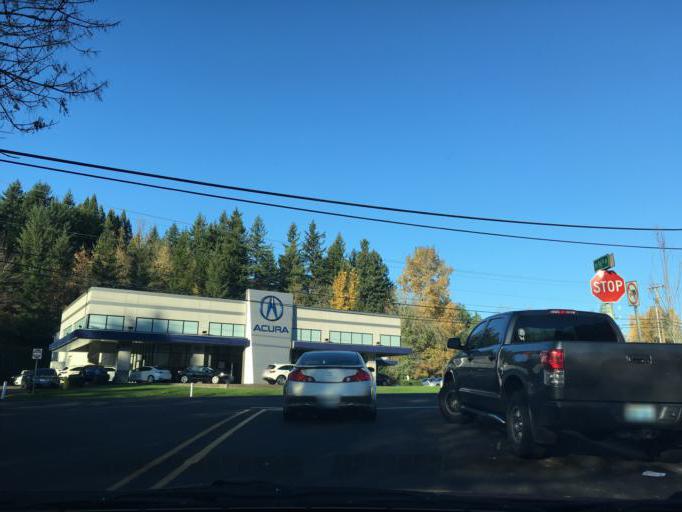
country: US
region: Oregon
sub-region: Washington County
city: West Slope
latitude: 45.4938
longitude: -122.7753
